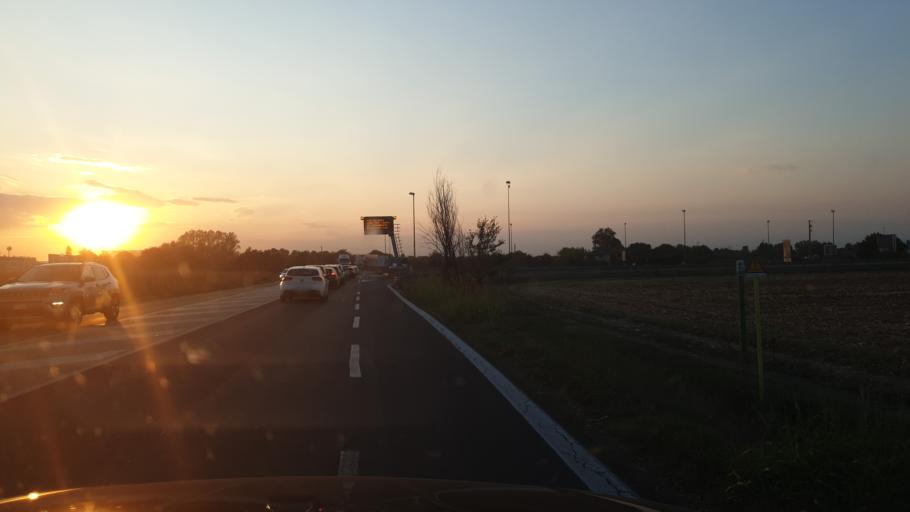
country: IT
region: Emilia-Romagna
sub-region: Provincia di Bologna
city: Progresso
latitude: 44.5857
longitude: 11.4033
